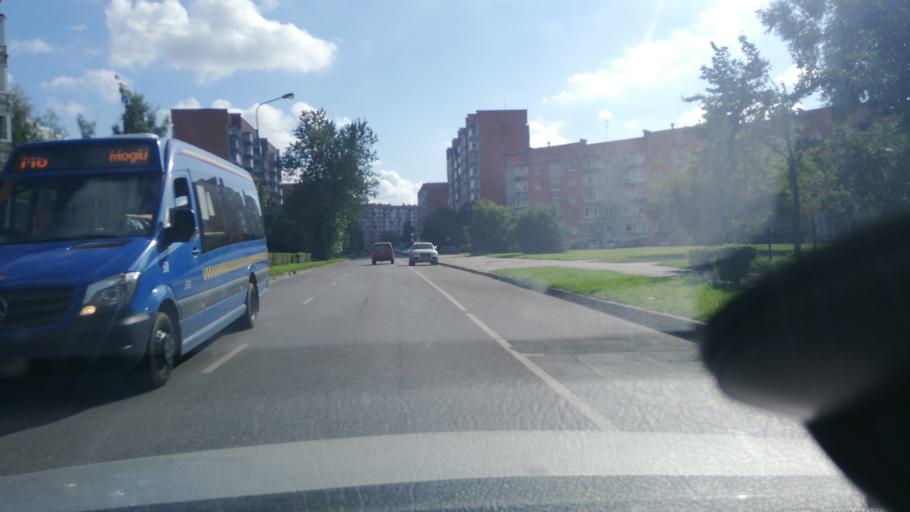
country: LT
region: Klaipedos apskritis
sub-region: Klaipeda
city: Klaipeda
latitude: 55.6703
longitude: 21.1994
